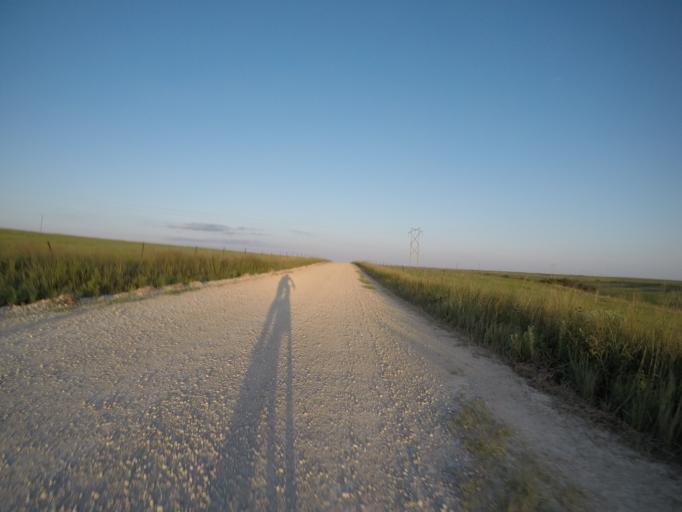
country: US
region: Kansas
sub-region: Riley County
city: Ogden
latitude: 39.0078
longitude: -96.6306
